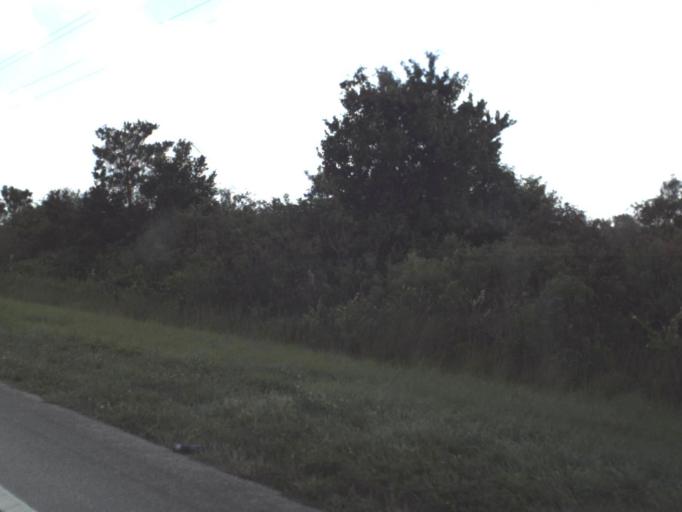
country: US
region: Florida
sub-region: Highlands County
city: Lake Placid
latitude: 27.4308
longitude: -81.2256
